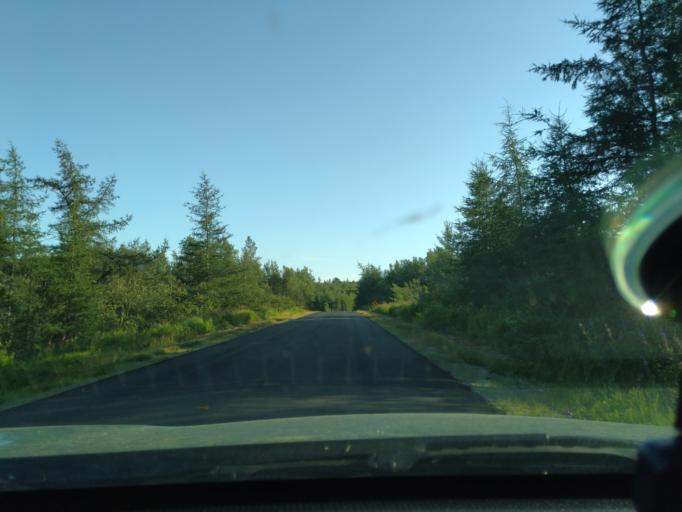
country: US
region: Maine
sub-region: Washington County
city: Eastport
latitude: 44.7207
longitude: -67.1342
